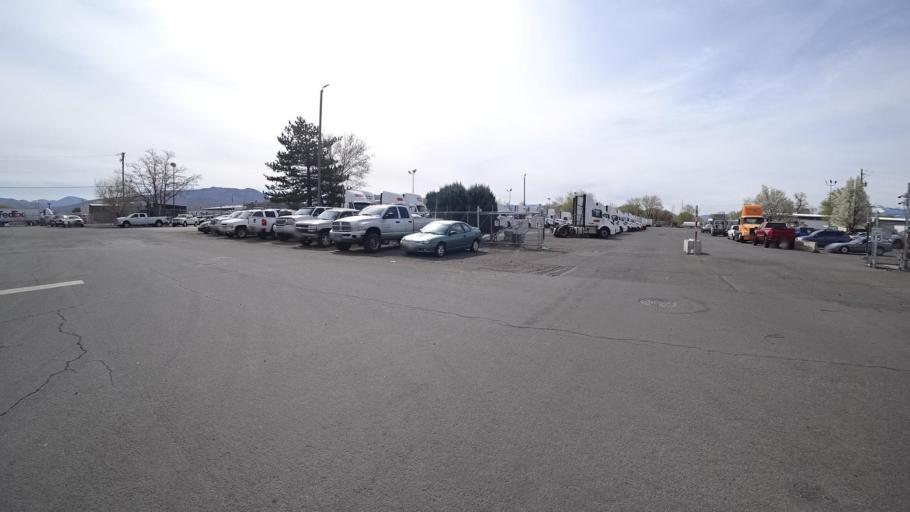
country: US
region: Nevada
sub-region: Washoe County
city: Sparks
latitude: 39.5198
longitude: -119.7588
